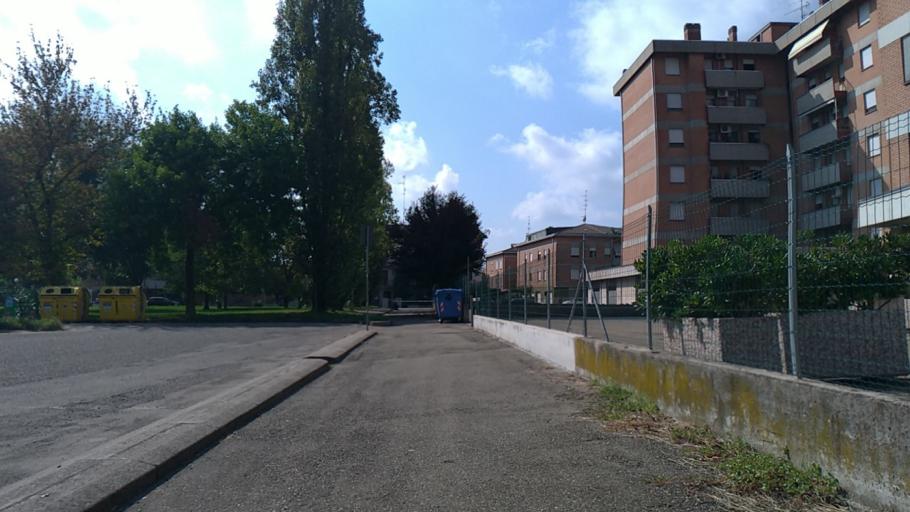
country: IT
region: Emilia-Romagna
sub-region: Provincia di Modena
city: Carpi Centro
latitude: 44.7728
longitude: 10.8692
